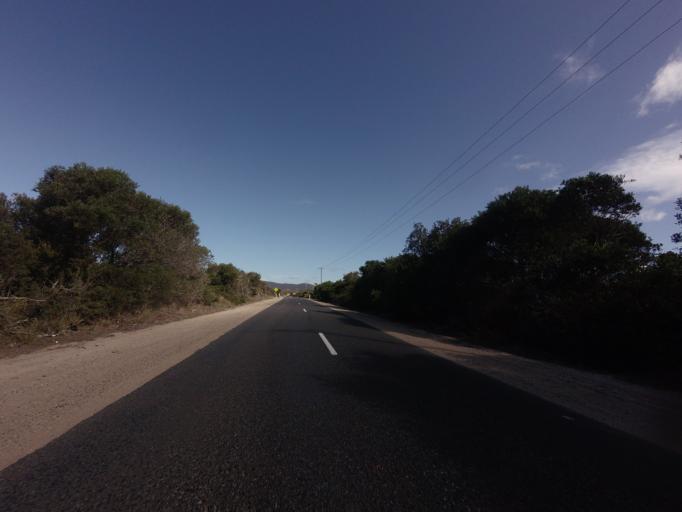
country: AU
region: Tasmania
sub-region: Break O'Day
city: St Helens
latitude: -41.8122
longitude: 148.2628
